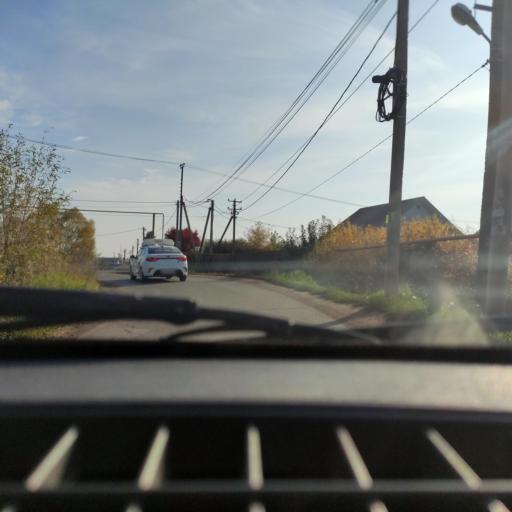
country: RU
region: Bashkortostan
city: Avdon
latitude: 54.6495
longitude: 55.7776
